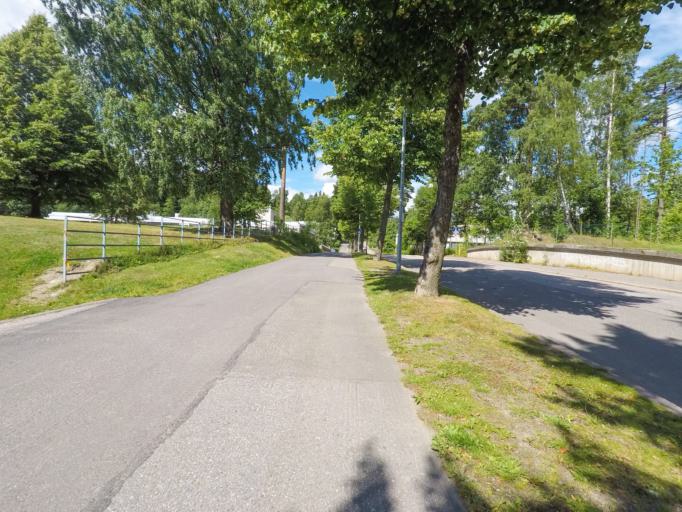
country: FI
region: Uusimaa
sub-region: Helsinki
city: Vantaa
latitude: 60.2189
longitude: 25.0926
